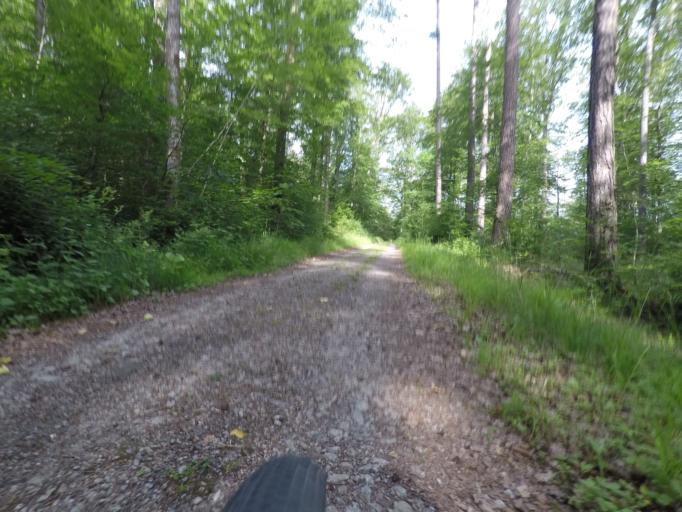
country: DE
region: Baden-Wuerttemberg
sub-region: Tuebingen Region
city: Tuebingen
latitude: 48.5541
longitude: 9.0624
